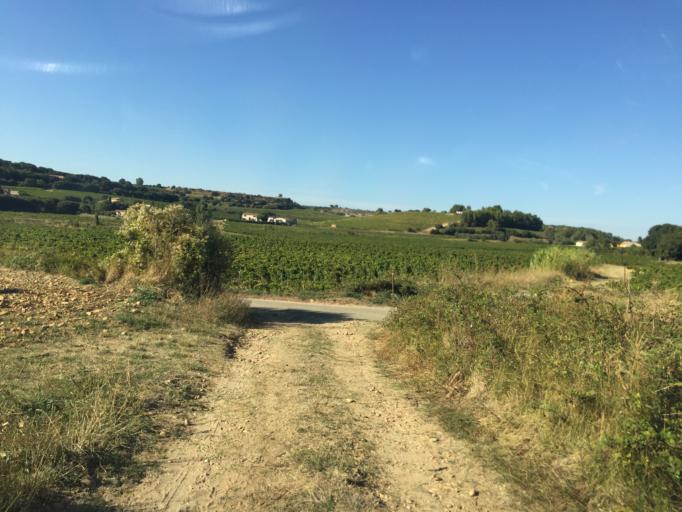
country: FR
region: Provence-Alpes-Cote d'Azur
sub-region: Departement du Vaucluse
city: Chateauneuf-du-Pape
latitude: 44.0584
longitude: 4.8440
